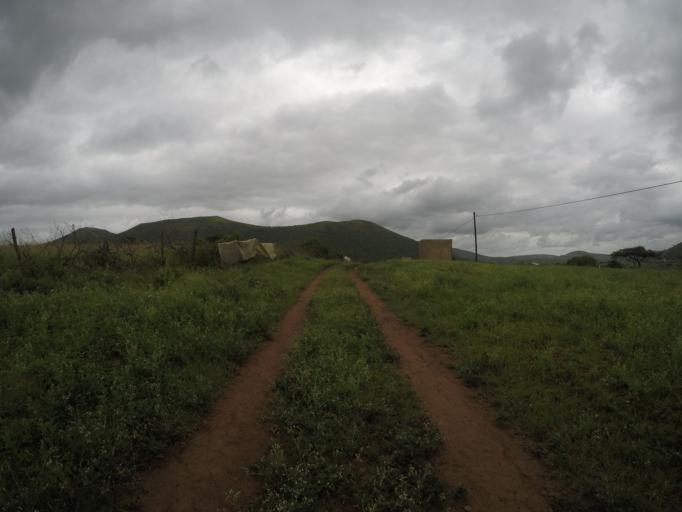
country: ZA
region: KwaZulu-Natal
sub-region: uThungulu District Municipality
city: Empangeni
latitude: -28.5862
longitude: 31.8639
